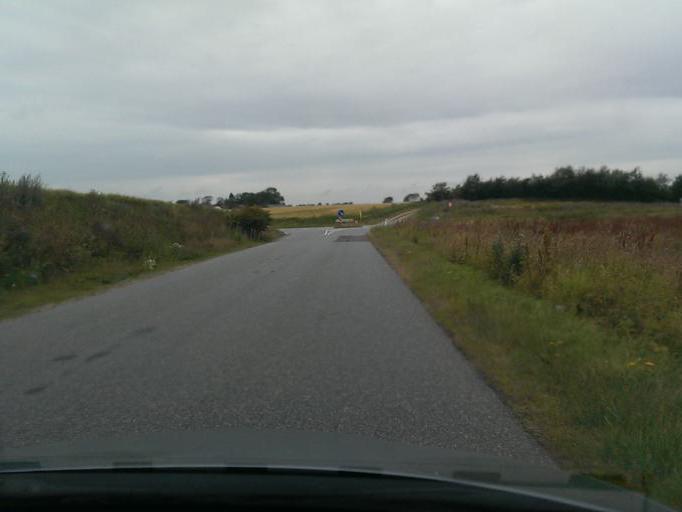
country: DK
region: North Denmark
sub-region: Hjorring Kommune
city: Vra
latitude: 57.3567
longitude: 9.9262
